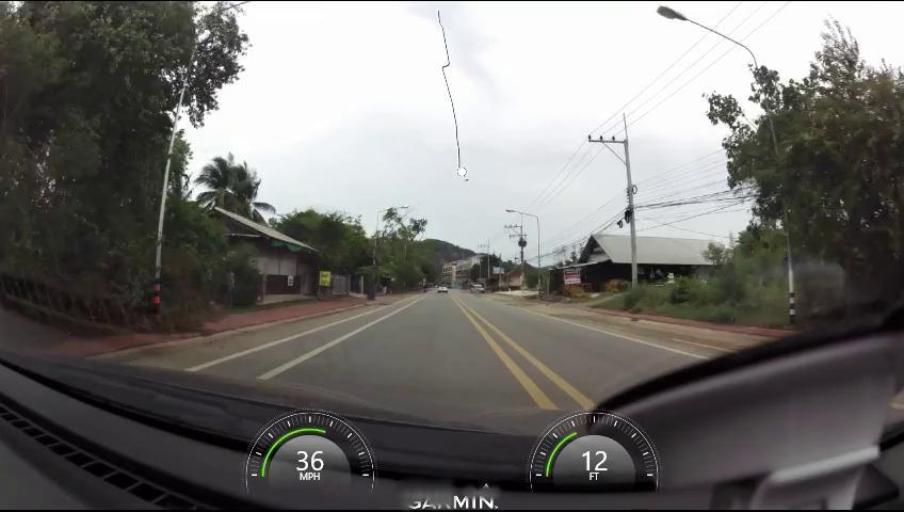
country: TH
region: Prachuap Khiri Khan
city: Pran Buri
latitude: 12.4641
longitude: 99.9742
